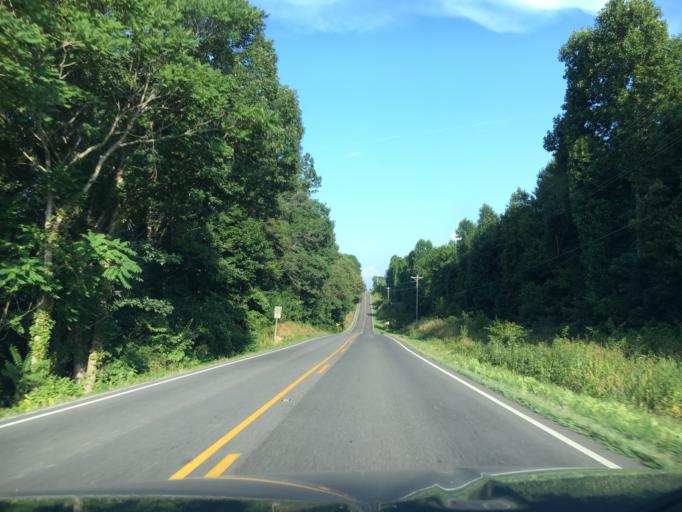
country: US
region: Virginia
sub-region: Franklin County
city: Union Hall
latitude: 36.9630
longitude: -79.5788
